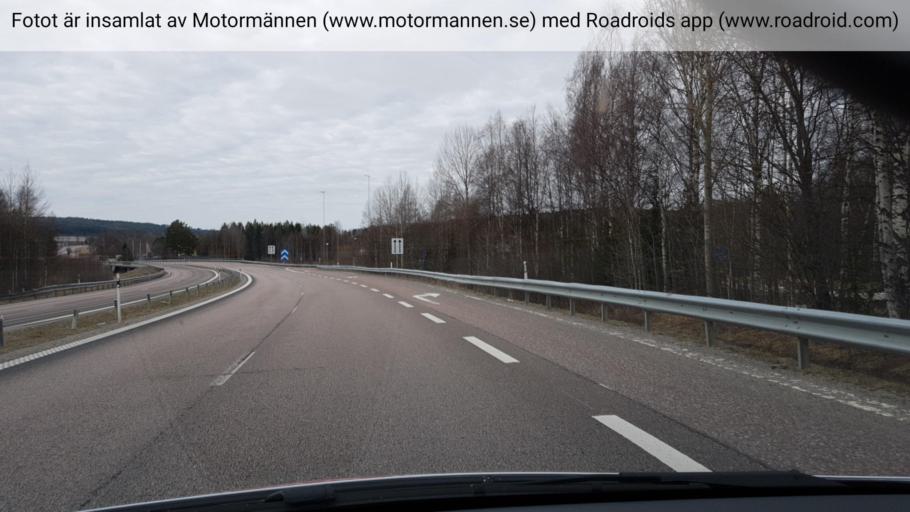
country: SE
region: Vaesternorrland
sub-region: OErnskoeldsviks Kommun
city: Ornskoldsvik
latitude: 63.3161
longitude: 18.7981
